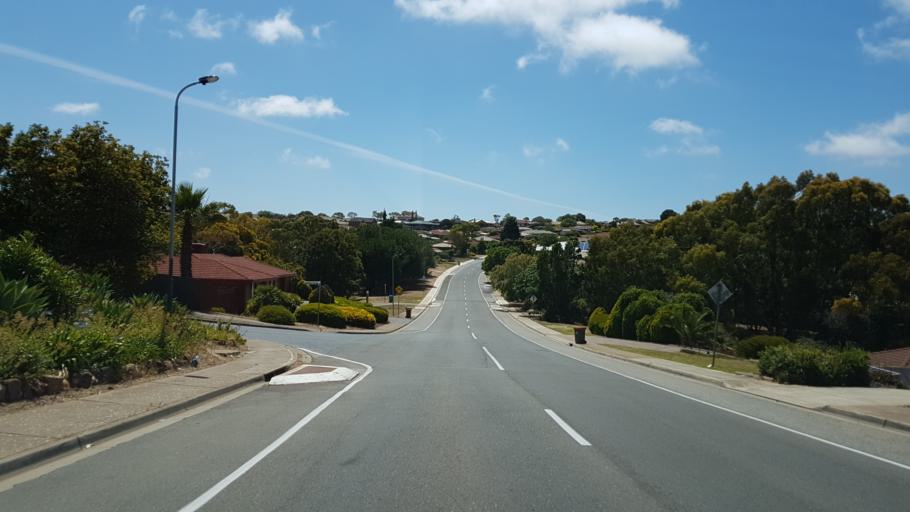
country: AU
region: South Australia
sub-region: Marion
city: Happy Valley
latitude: -35.0677
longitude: 138.5216
